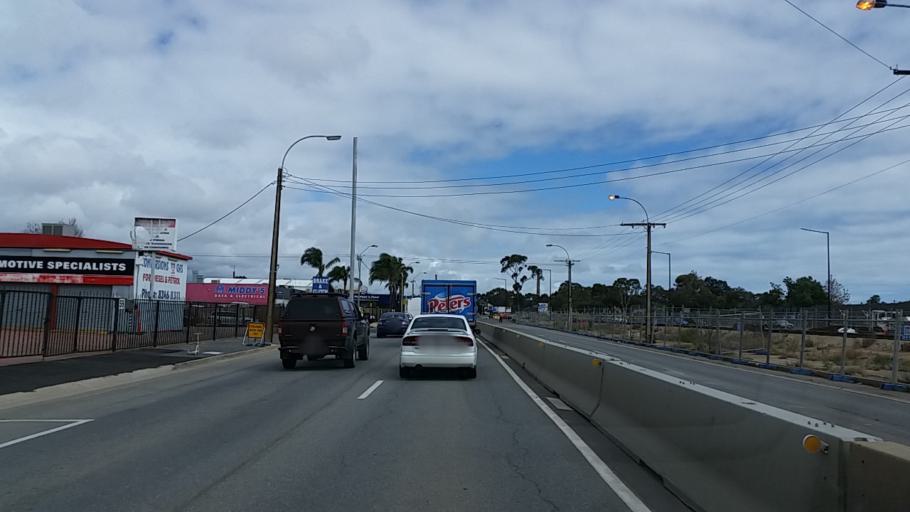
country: AU
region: South Australia
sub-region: City of West Torrens
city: Thebarton
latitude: -34.9072
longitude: 138.5654
